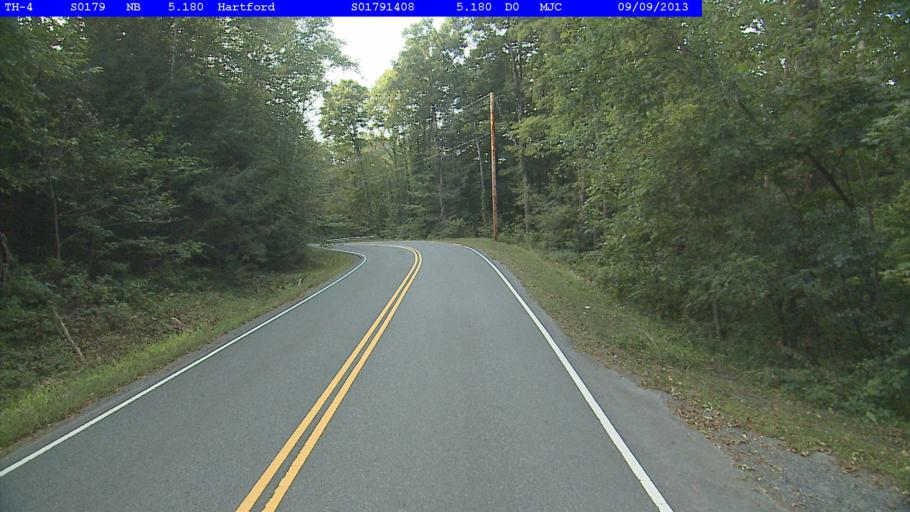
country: US
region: Vermont
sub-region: Windsor County
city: White River Junction
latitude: 43.7033
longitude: -72.4189
